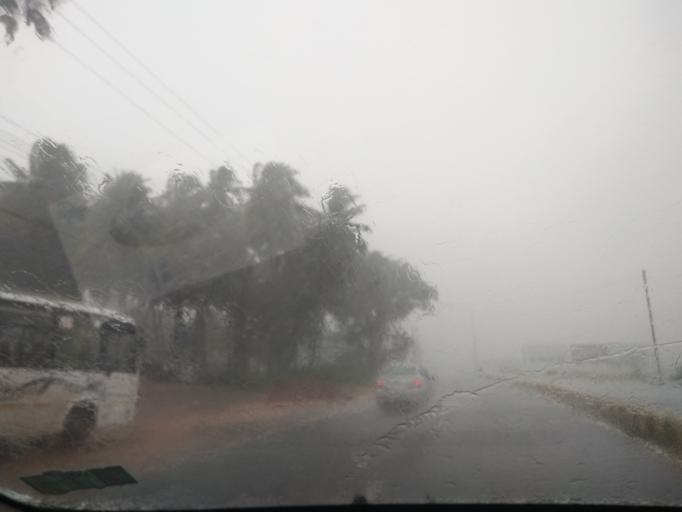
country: IN
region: Goa
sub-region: North Goa
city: Bambolim
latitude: 15.4733
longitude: 73.8501
